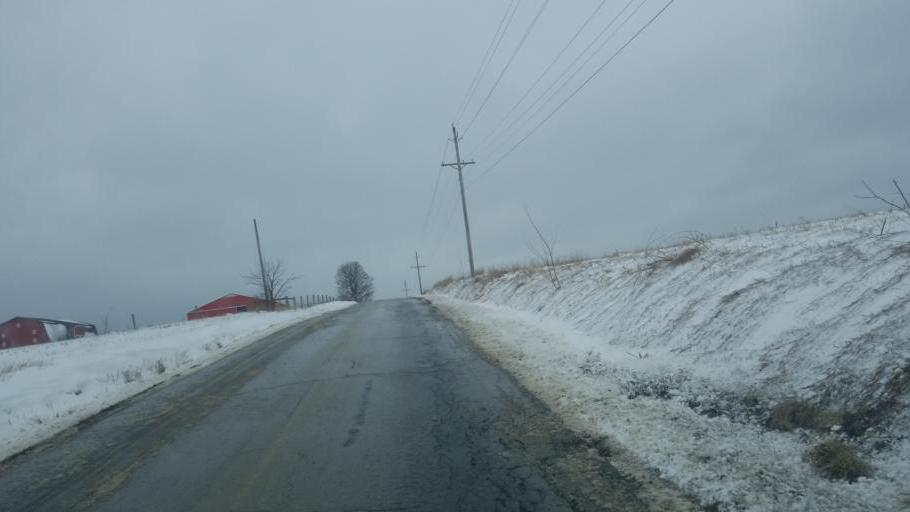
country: US
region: Ohio
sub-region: Knox County
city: Oak Hill
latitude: 40.4734
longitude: -82.1292
